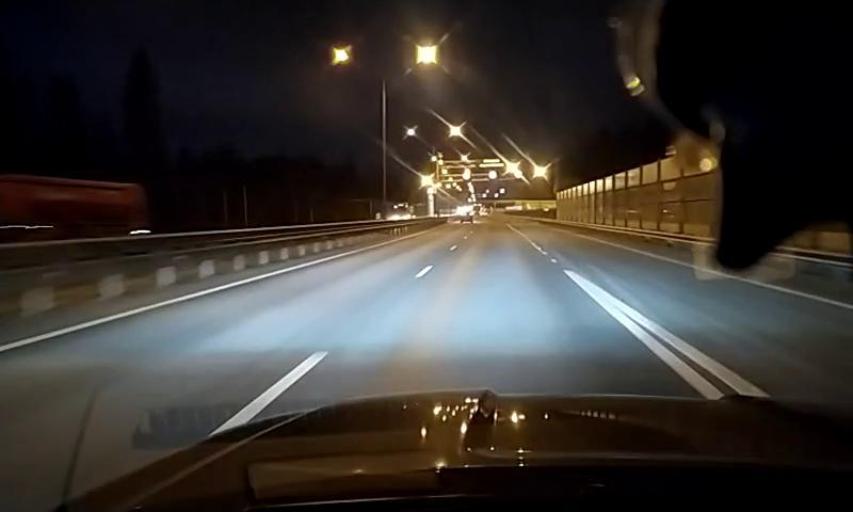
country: RU
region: Leningrad
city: Agalatovo
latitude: 60.2270
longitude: 30.3579
